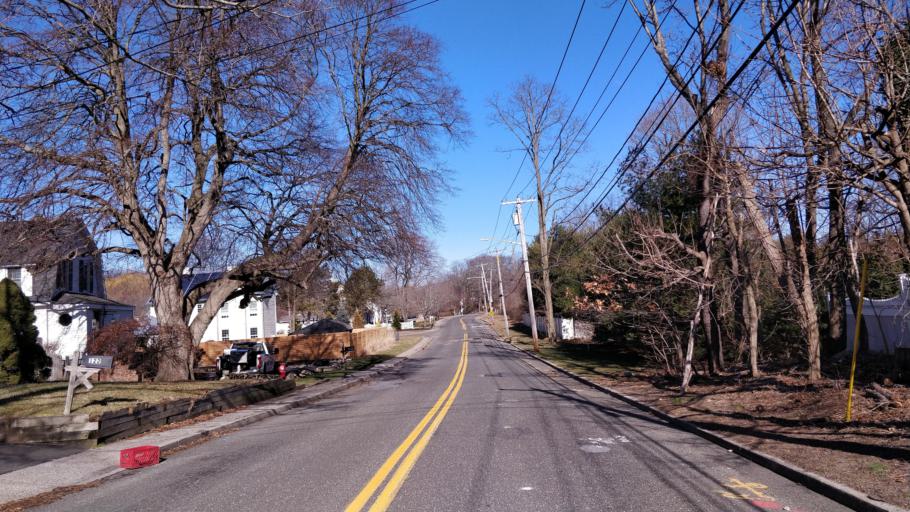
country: US
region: New York
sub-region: Suffolk County
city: Saint James
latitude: 40.8898
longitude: -73.1460
